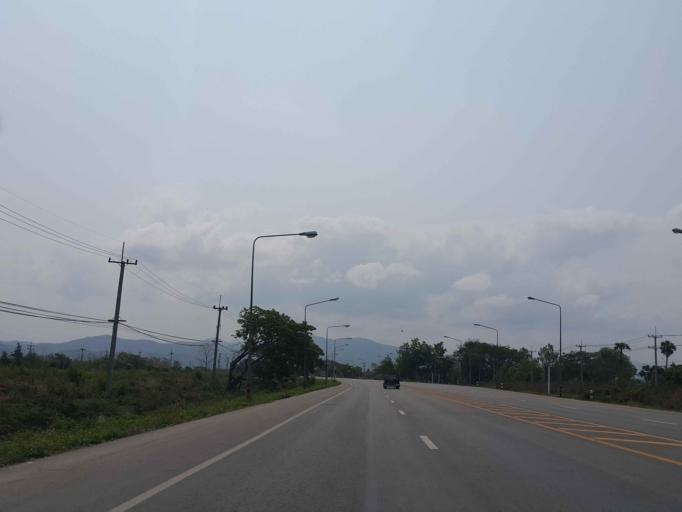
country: TH
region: Chiang Mai
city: San Kamphaeng
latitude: 18.7138
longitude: 99.1218
